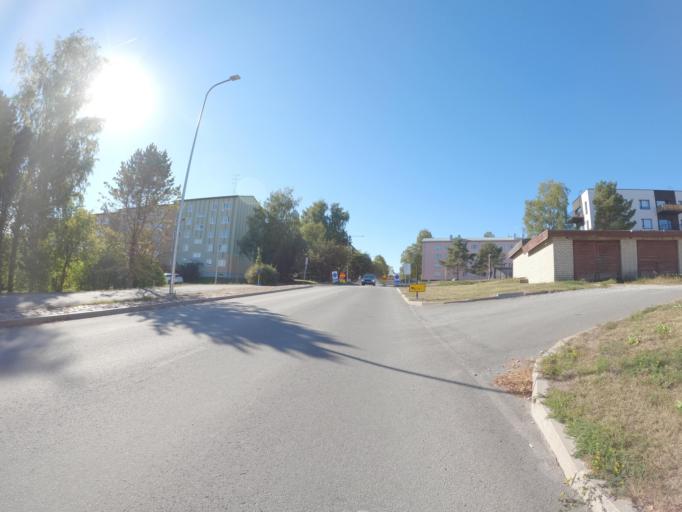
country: EE
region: Raplamaa
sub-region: Rapla vald
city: Rapla
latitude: 58.9990
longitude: 24.7966
